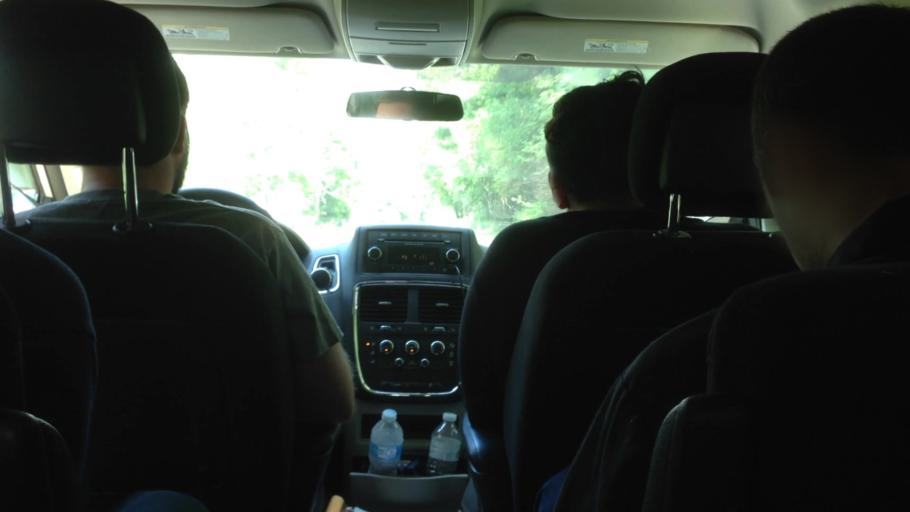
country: US
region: New York
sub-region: Dutchess County
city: Tivoli
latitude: 42.0905
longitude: -73.8957
